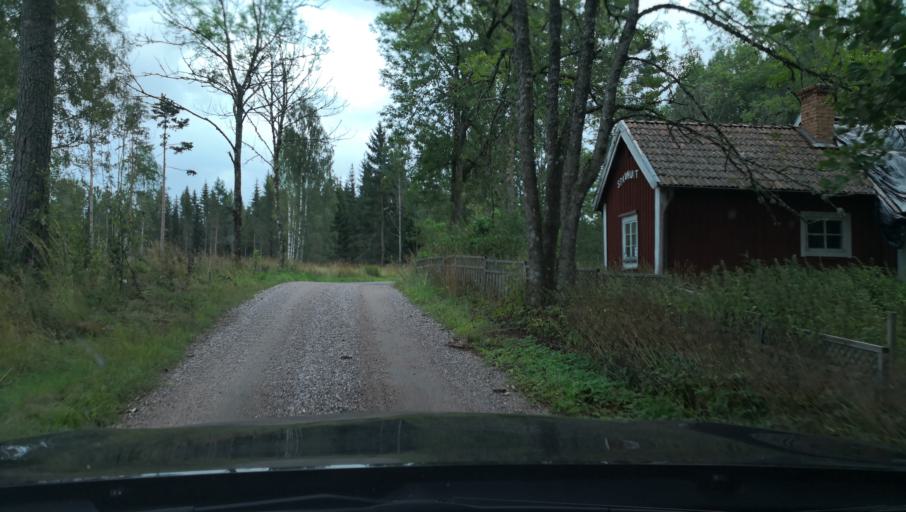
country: SE
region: Vaestmanland
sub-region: Arboga Kommun
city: Tyringe
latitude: 59.3594
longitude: 15.9967
